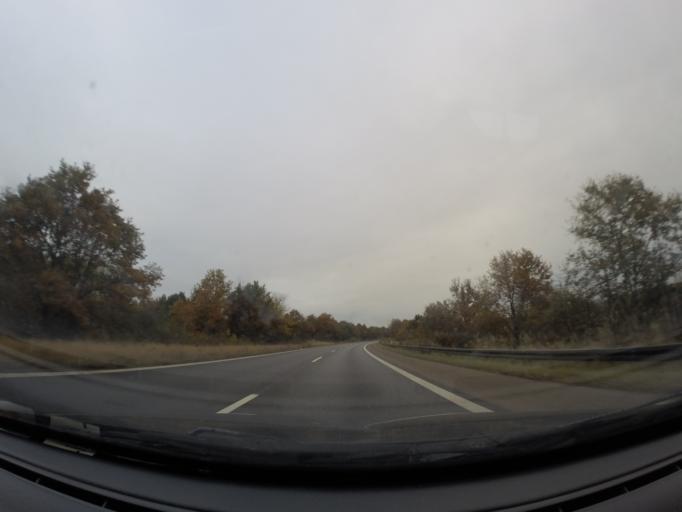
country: DK
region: Capital Region
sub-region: Hoje-Taastrup Kommune
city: Taastrup
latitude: 55.6638
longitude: 12.3138
